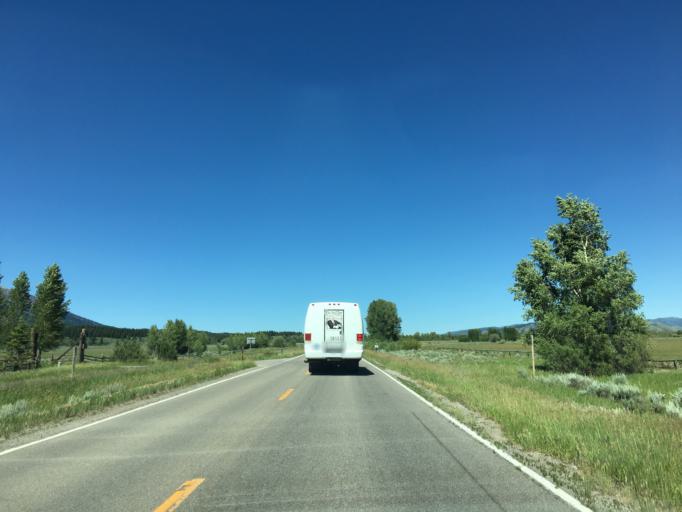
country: US
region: Wyoming
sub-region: Teton County
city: Moose Wilson Road
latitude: 43.5886
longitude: -110.8164
